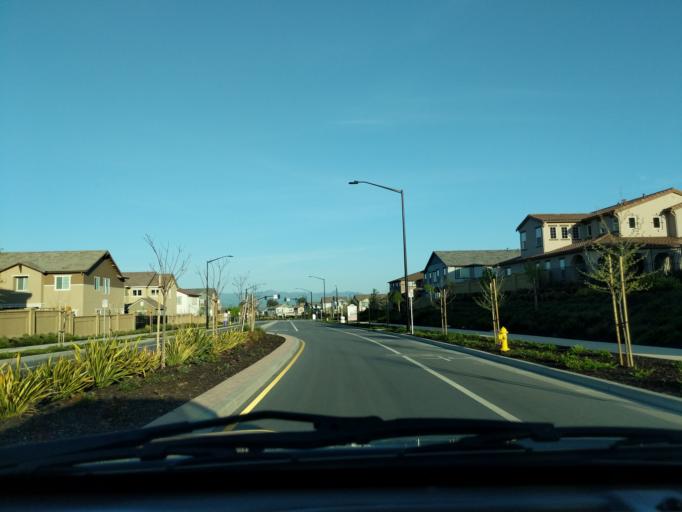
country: US
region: California
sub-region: Santa Clara County
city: Gilroy
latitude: 36.9894
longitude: -121.5836
